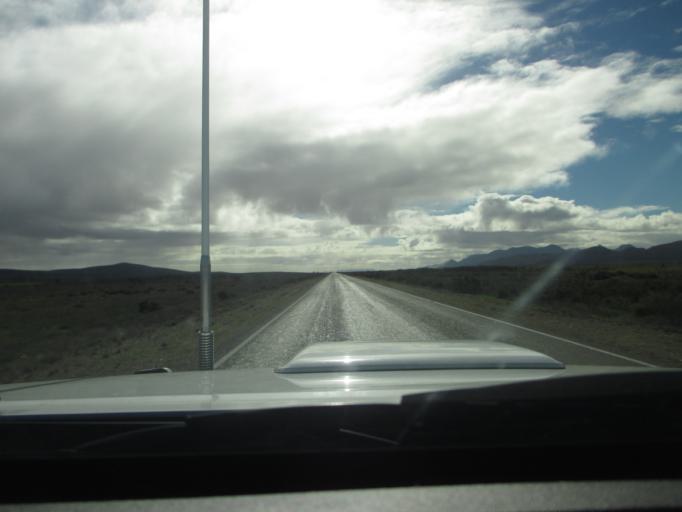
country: AU
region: South Australia
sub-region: Flinders Ranges
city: Quorn
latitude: -31.6657
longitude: 138.3729
